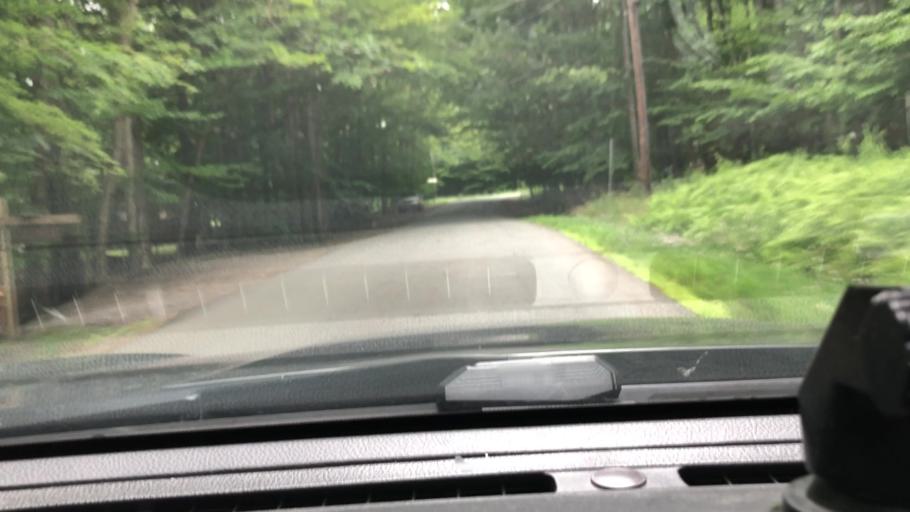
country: US
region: Pennsylvania
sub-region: Lackawanna County
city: Moscow
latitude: 41.2509
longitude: -75.4851
